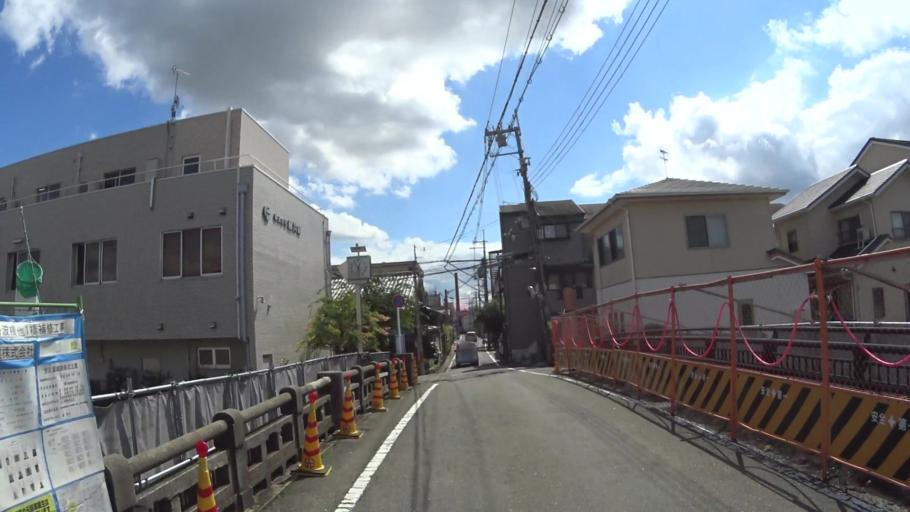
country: JP
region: Kyoto
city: Muko
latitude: 34.9372
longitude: 135.7573
